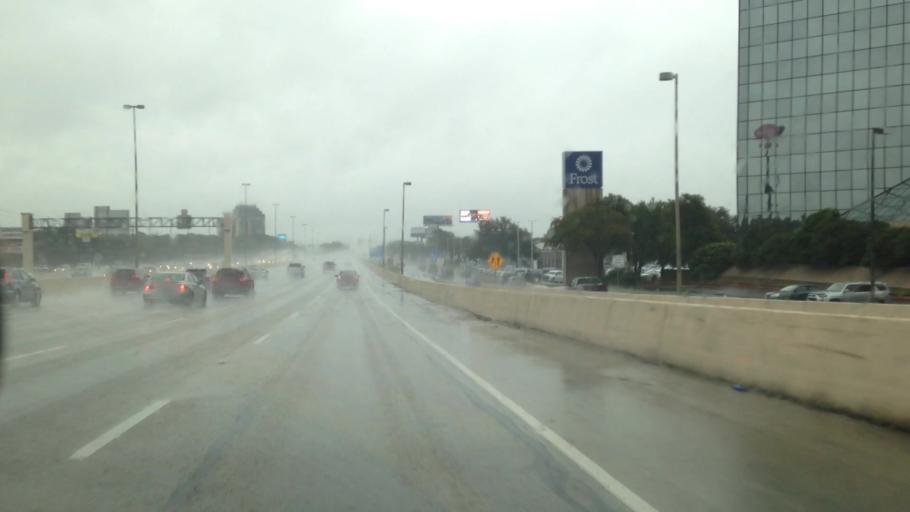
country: US
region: Texas
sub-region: Bexar County
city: Alamo Heights
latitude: 29.5170
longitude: -98.4501
